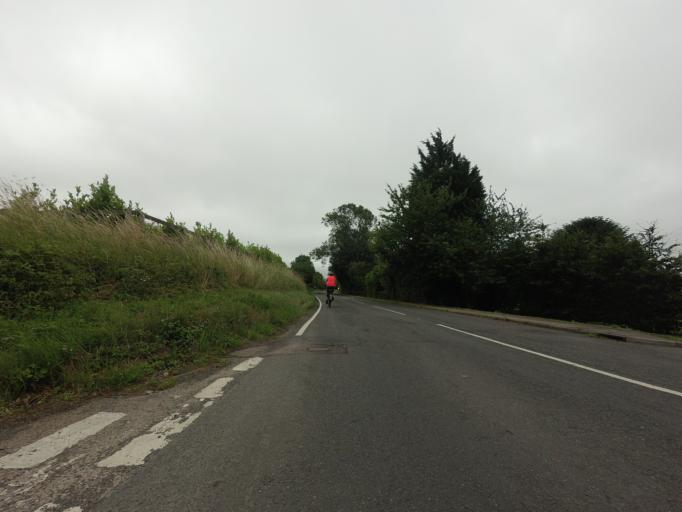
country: GB
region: England
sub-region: Kent
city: Meopham
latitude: 51.3800
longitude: 0.3520
